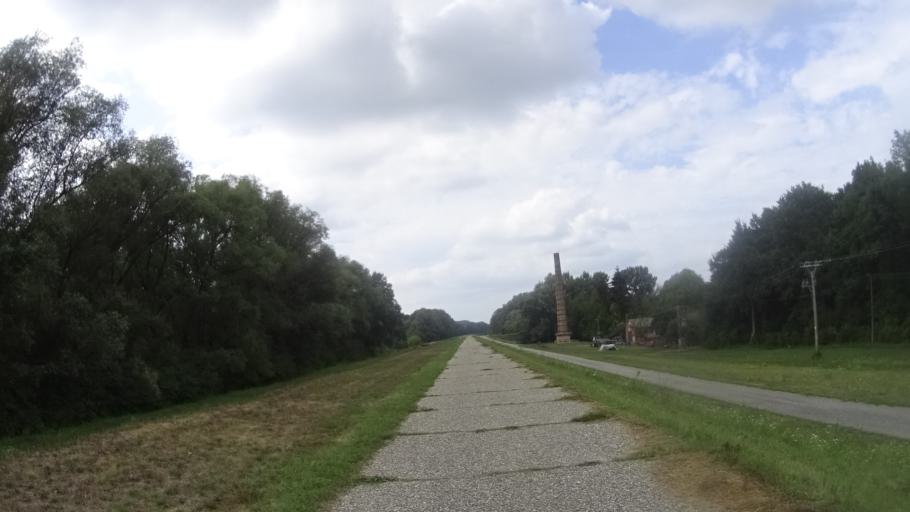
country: SK
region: Trnavsky
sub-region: Okres Dunajska Streda
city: Velky Meder
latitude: 47.7642
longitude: 17.7304
